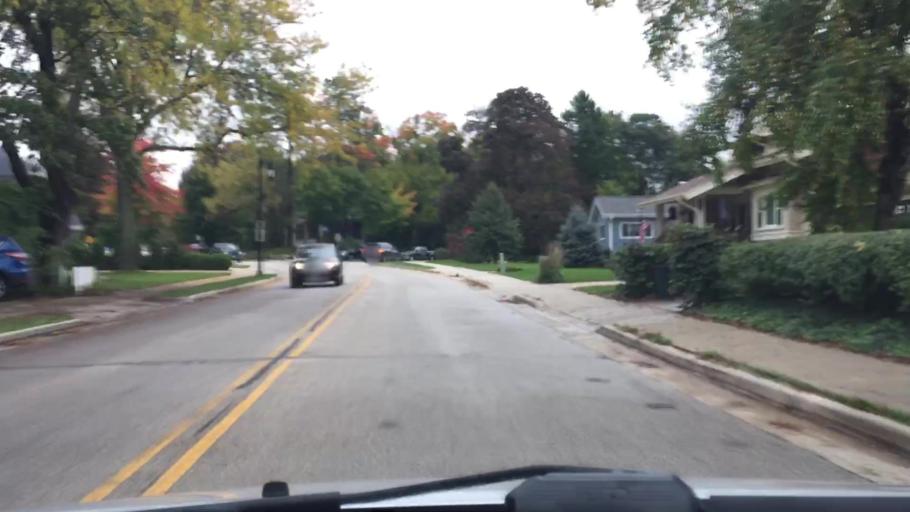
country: US
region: Wisconsin
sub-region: Waukesha County
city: Oconomowoc
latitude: 43.1180
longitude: -88.4993
